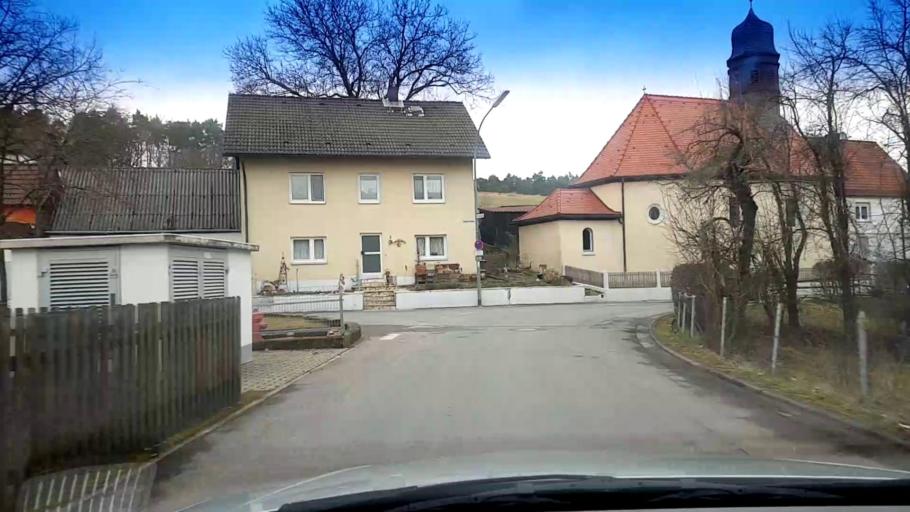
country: DE
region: Bavaria
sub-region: Upper Franconia
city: Bischberg
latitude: 49.8994
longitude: 10.8061
